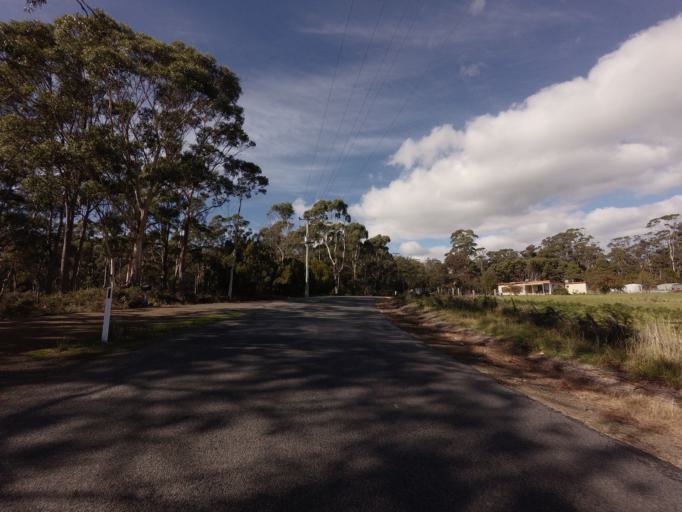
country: AU
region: Tasmania
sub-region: Clarence
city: Sandford
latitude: -43.0273
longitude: 147.7264
